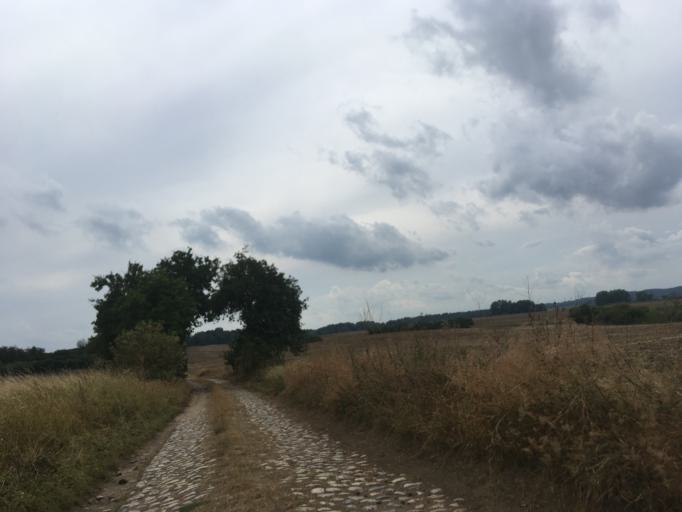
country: DE
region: Brandenburg
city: Chorin
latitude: 52.9509
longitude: 13.8875
